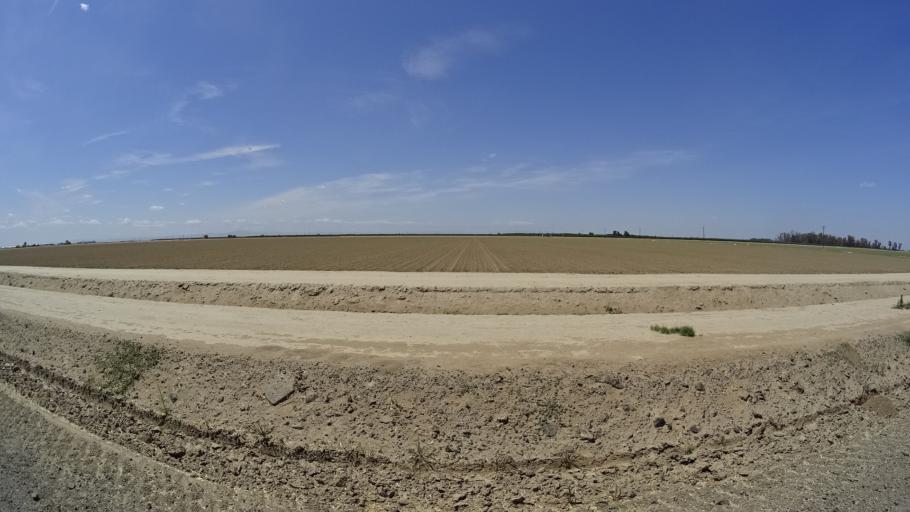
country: US
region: California
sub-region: Kings County
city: Home Garden
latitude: 36.2464
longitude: -119.6728
